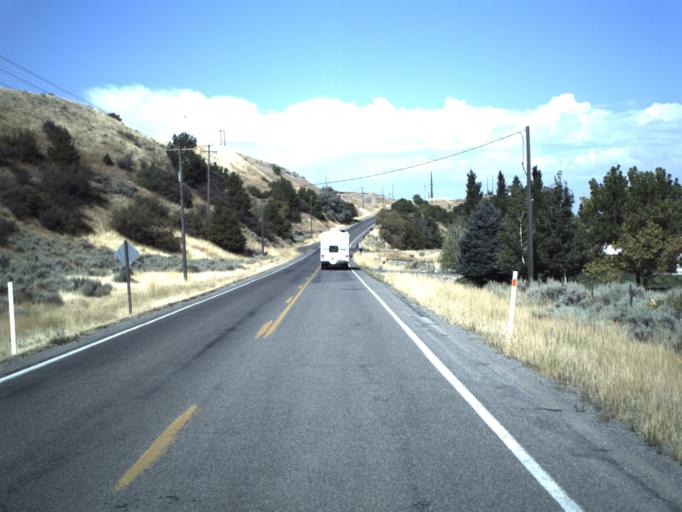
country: US
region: Utah
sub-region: Cache County
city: Hyrum
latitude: 41.6291
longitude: -111.8075
